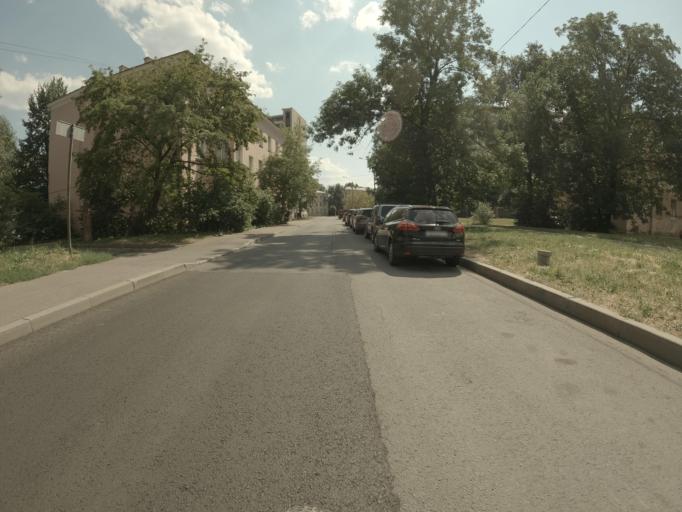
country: RU
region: St.-Petersburg
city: Avtovo
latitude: 59.8930
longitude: 30.2613
